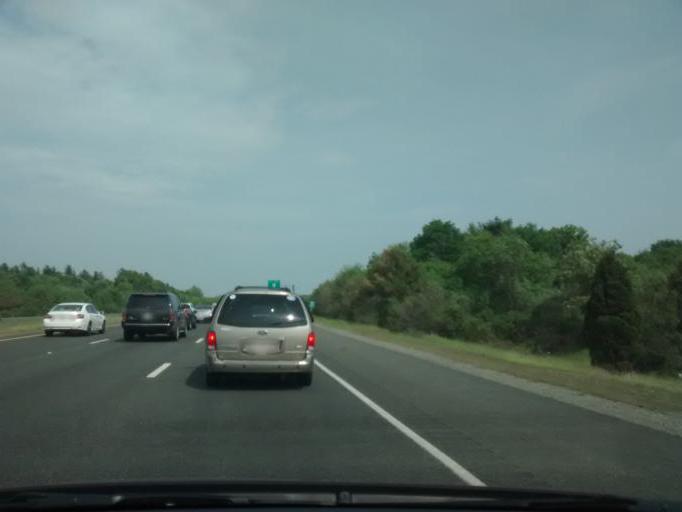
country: US
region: Massachusetts
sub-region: Bristol County
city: Raynham
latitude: 41.9568
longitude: -71.0416
